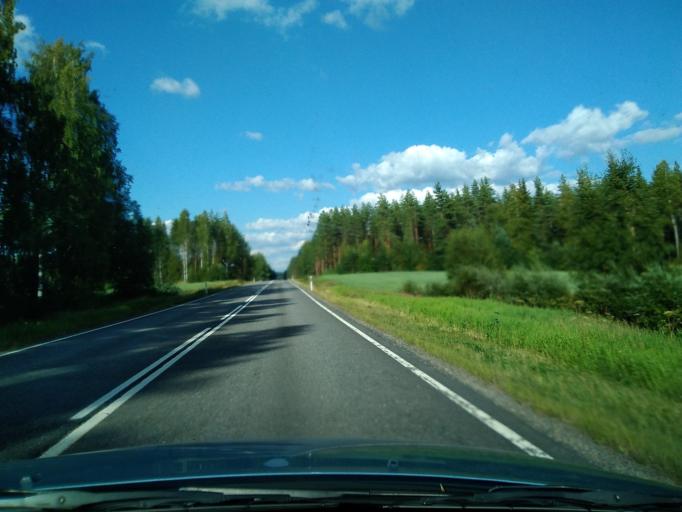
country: FI
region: Pirkanmaa
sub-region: Ylae-Pirkanmaa
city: Maenttae
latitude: 61.9644
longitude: 24.5936
